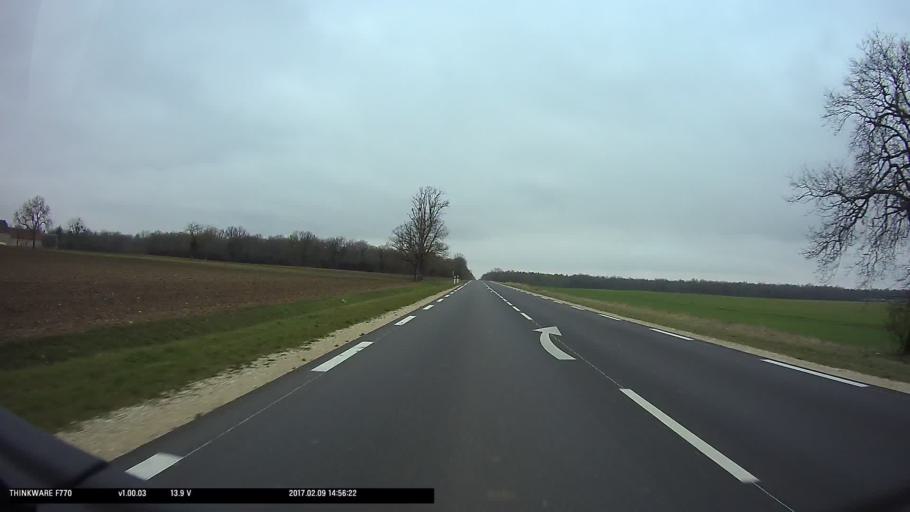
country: FR
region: Centre
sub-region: Departement du Cher
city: Levet
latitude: 46.8669
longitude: 2.4185
